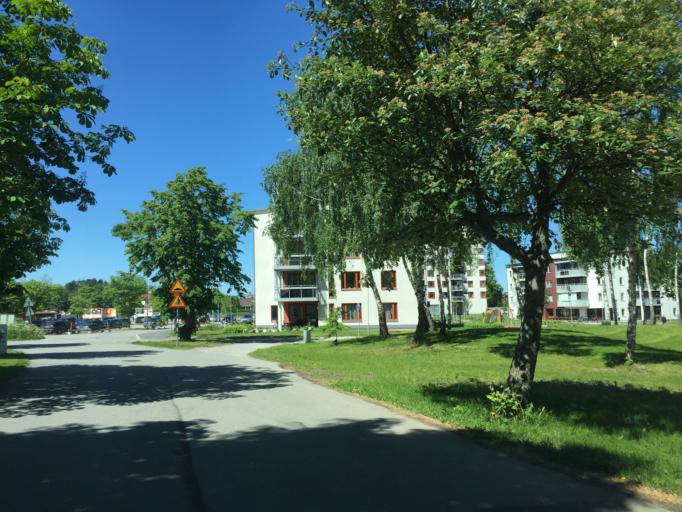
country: SE
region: OErebro
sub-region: Orebro Kommun
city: Orebro
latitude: 59.2469
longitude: 15.1695
